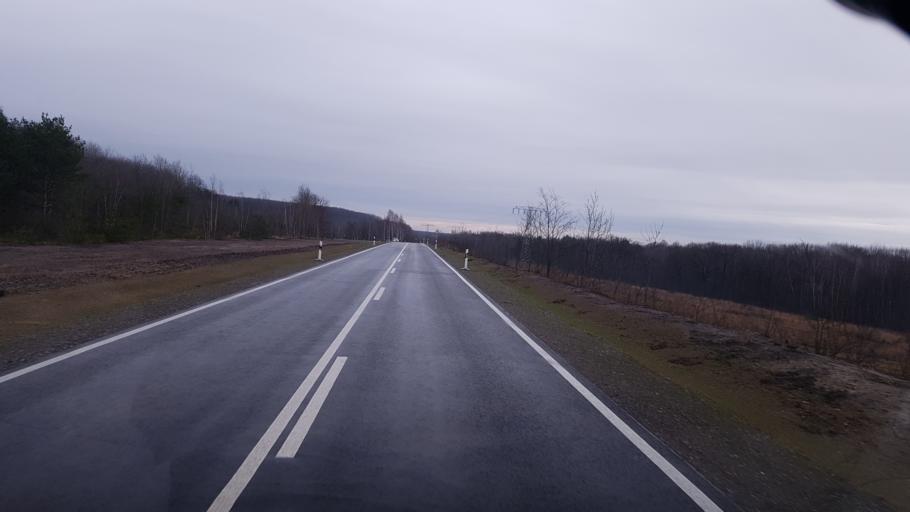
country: DE
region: Brandenburg
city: Lauchhammer
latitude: 51.5147
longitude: 13.7961
